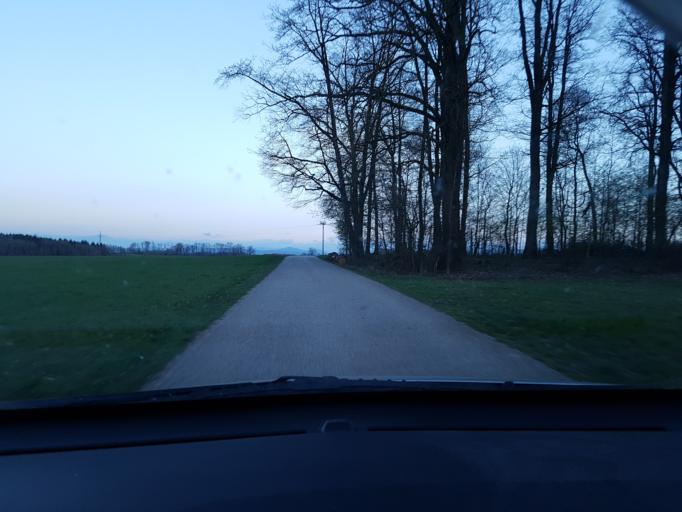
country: AT
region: Upper Austria
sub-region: Politischer Bezirk Linz-Land
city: Ansfelden
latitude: 48.1731
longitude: 14.3206
